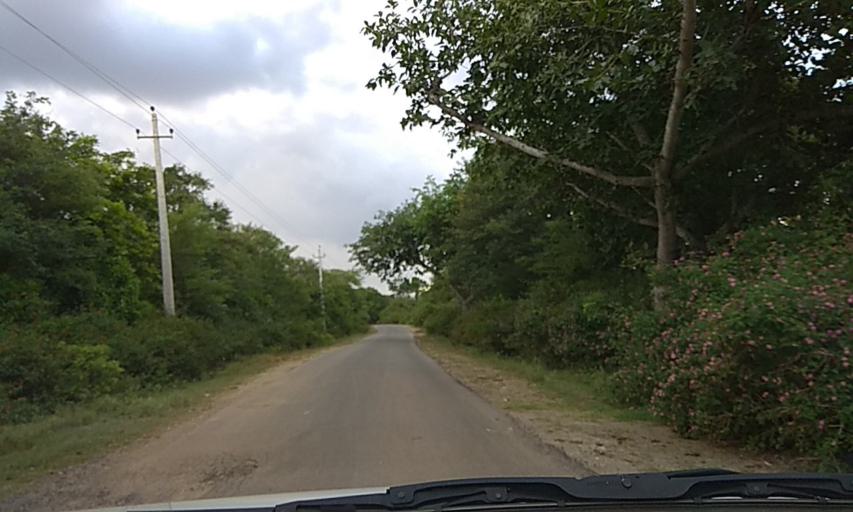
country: IN
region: Karnataka
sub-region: Chamrajnagar
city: Gundlupet
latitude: 11.8716
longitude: 76.7385
